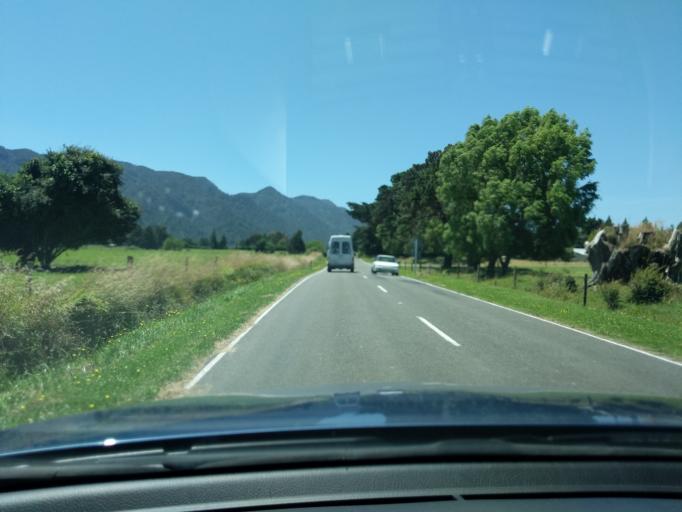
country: NZ
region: Tasman
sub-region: Tasman District
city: Takaka
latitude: -40.7008
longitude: 172.6321
